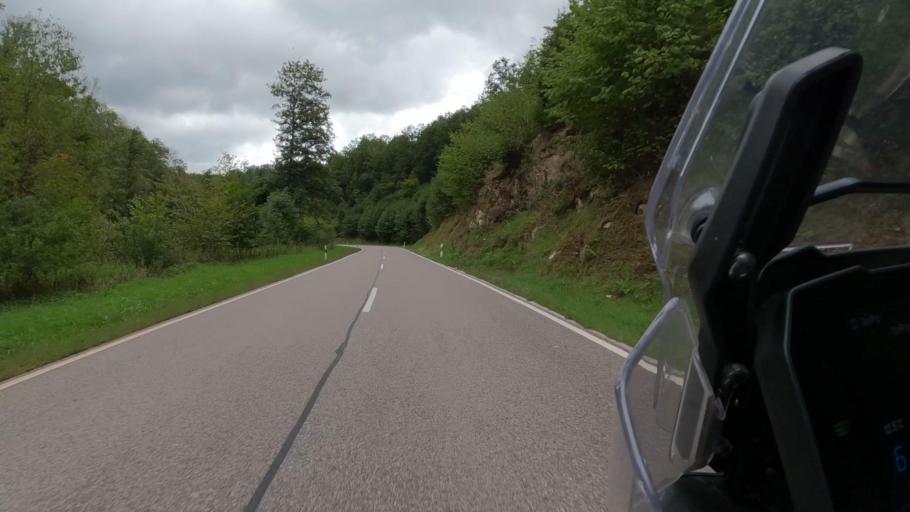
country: DE
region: Baden-Wuerttemberg
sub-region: Freiburg Region
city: Uhlingen-Birkendorf
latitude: 47.7148
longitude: 8.3457
